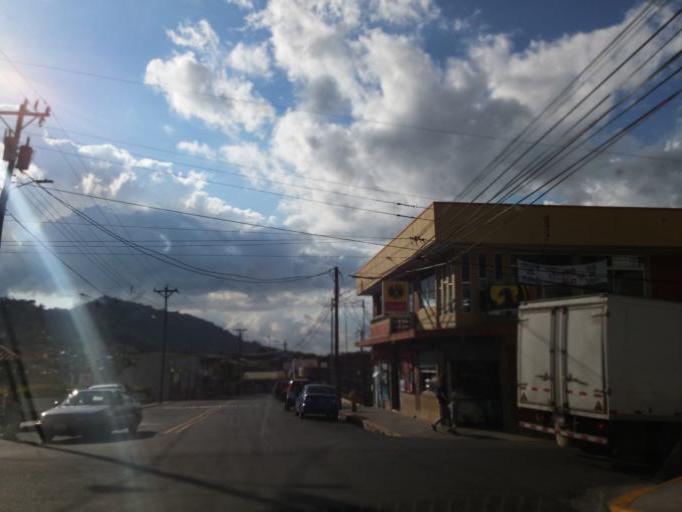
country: CR
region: San Jose
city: San Ignacio
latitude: 9.7990
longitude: -84.1622
